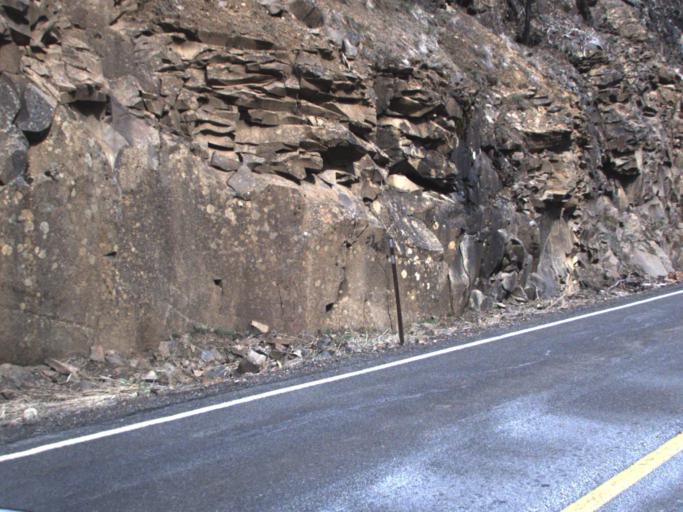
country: US
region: Washington
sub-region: Kittitas County
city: Cle Elum
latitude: 46.9854
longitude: -121.1182
